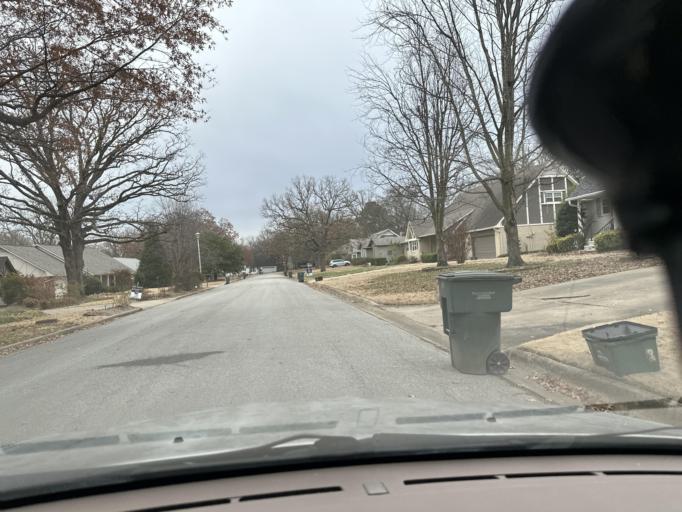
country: US
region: Arkansas
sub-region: Washington County
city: Johnson
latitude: 36.1048
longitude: -94.1432
